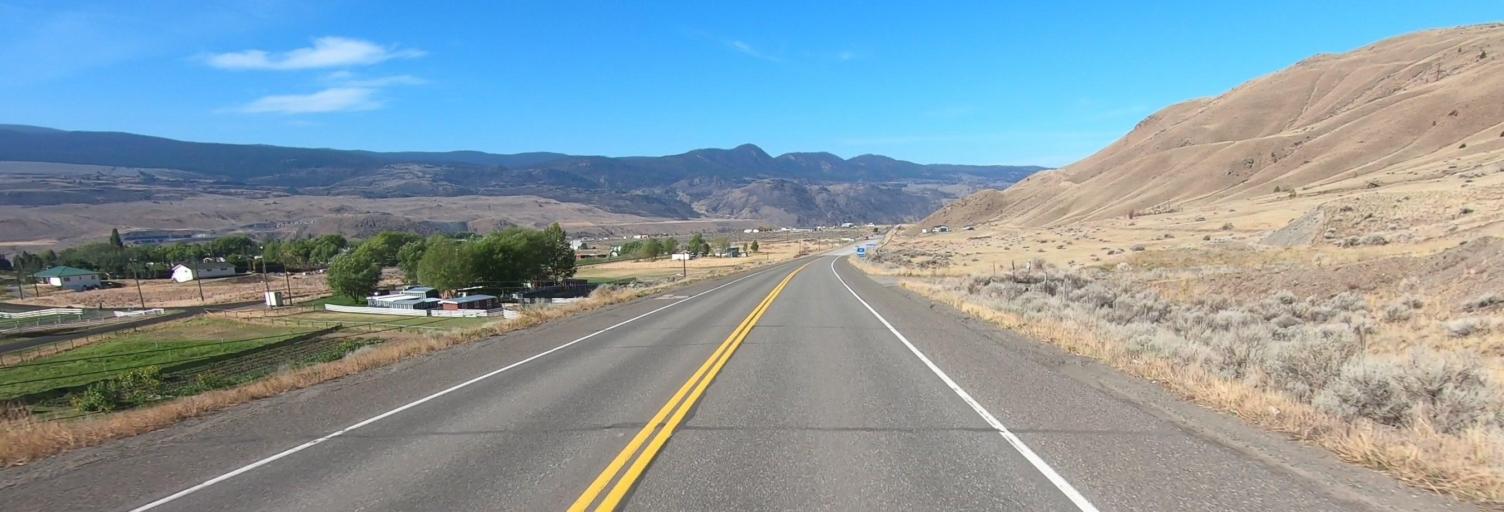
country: CA
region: British Columbia
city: Logan Lake
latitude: 50.7689
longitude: -120.9623
